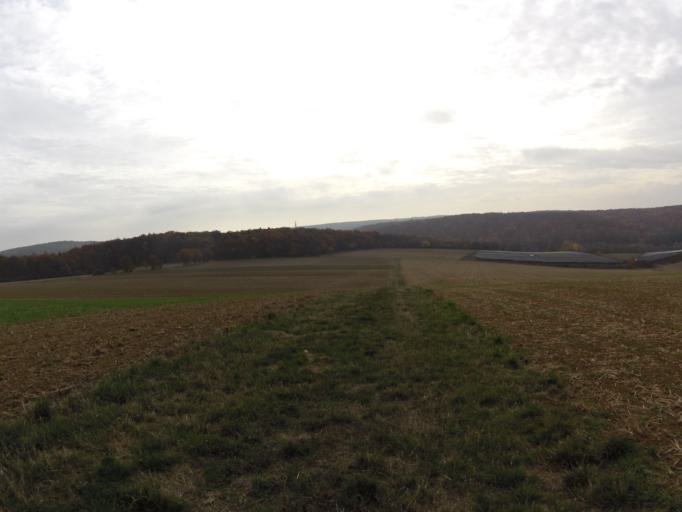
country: DE
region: Bavaria
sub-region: Regierungsbezirk Unterfranken
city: Waldbrunn
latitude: 49.7552
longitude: 9.8054
